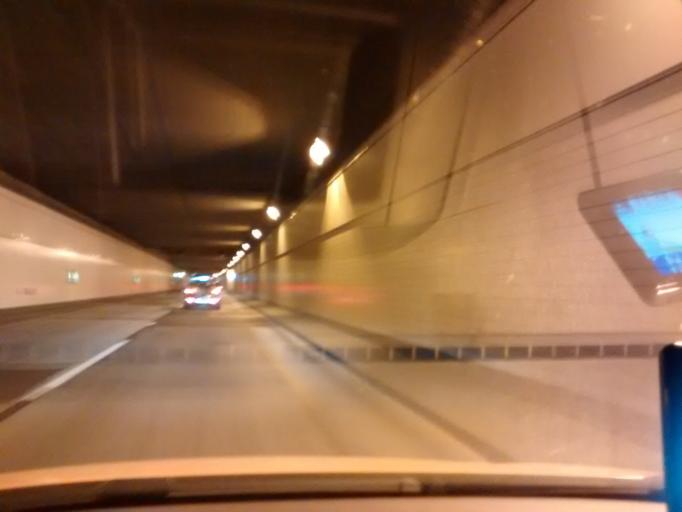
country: DE
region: Berlin
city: Tegel
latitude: 52.5868
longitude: 13.2913
